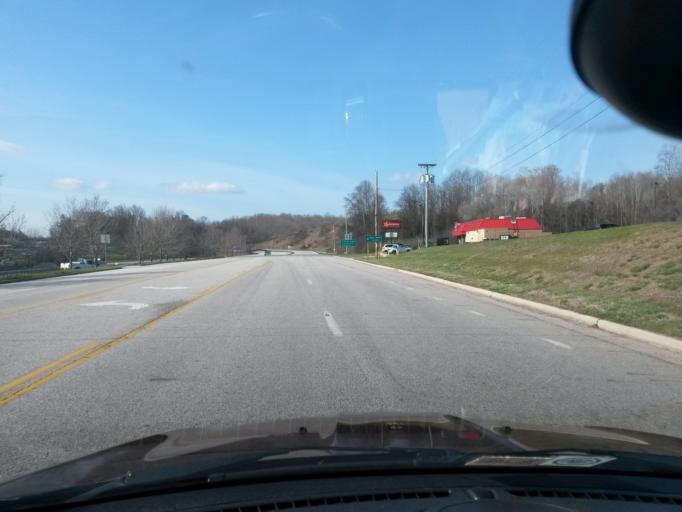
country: US
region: Virginia
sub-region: Amherst County
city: Amherst
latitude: 37.5641
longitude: -79.0637
